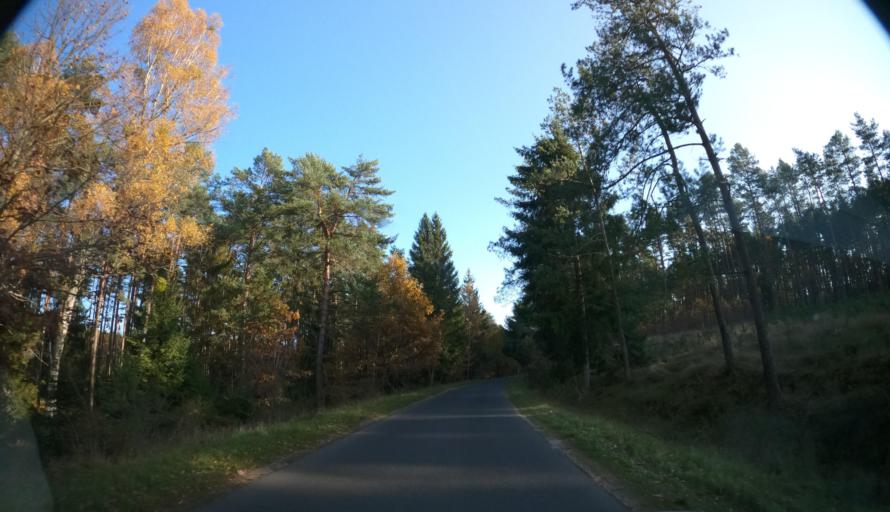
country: PL
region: Pomeranian Voivodeship
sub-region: Powiat slupski
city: Kepice
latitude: 54.2321
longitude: 16.7672
